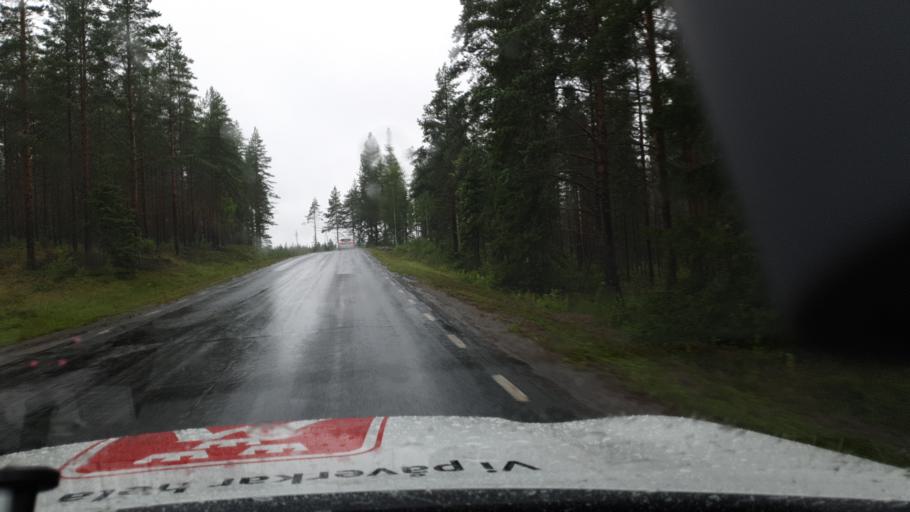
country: SE
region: Vaesterbotten
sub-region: Skelleftea Kommun
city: Burea
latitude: 64.6053
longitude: 21.1090
